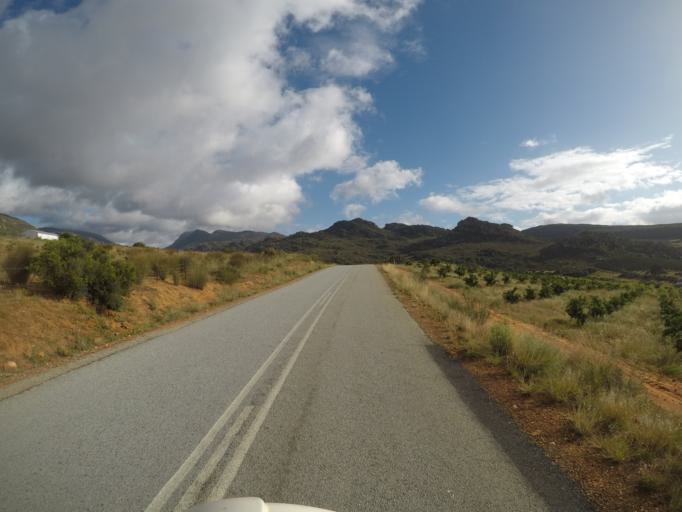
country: ZA
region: Western Cape
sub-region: West Coast District Municipality
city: Clanwilliam
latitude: -32.4248
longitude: 18.9347
